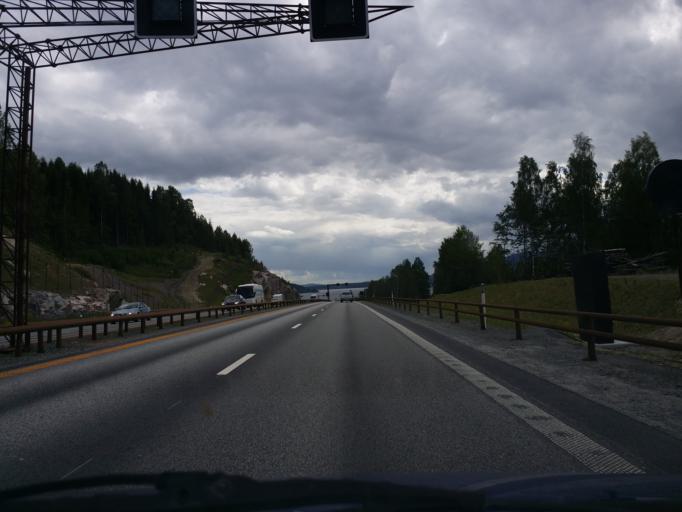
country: NO
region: Akershus
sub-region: Eidsvoll
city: Eidsvoll
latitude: 60.4922
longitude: 11.2364
